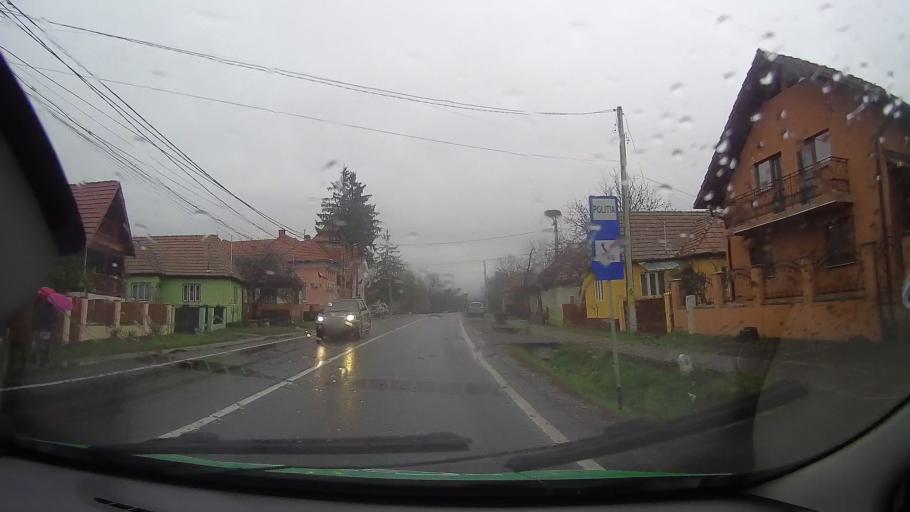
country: RO
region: Mures
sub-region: Comuna Brancovenesti
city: Brancovenesti
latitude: 46.8567
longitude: 24.7599
